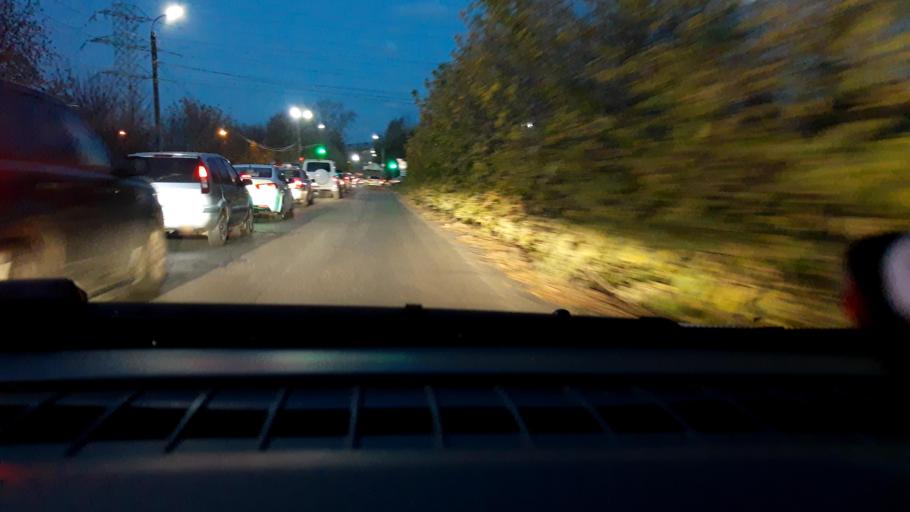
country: RU
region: Nizjnij Novgorod
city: Novaya Balakhna
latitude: 56.4876
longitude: 43.5949
